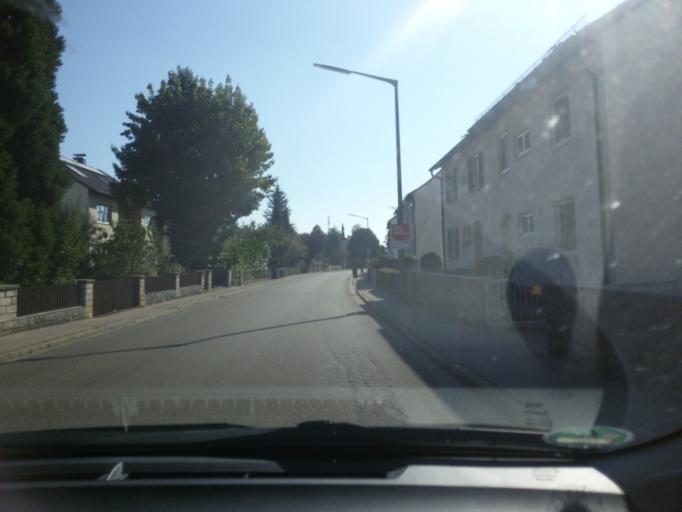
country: DE
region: Bavaria
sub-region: Regierungsbezirk Mittelfranken
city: Wassertrudingen
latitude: 49.0444
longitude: 10.6019
